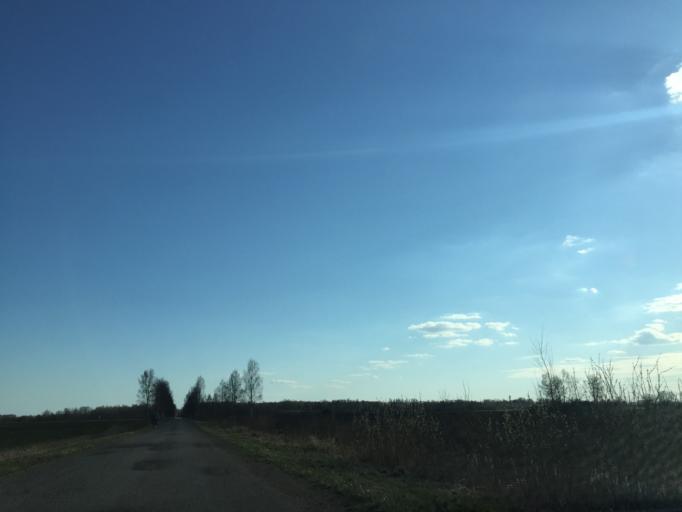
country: EE
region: Valgamaa
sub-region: Torva linn
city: Torva
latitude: 58.2436
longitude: 25.9477
